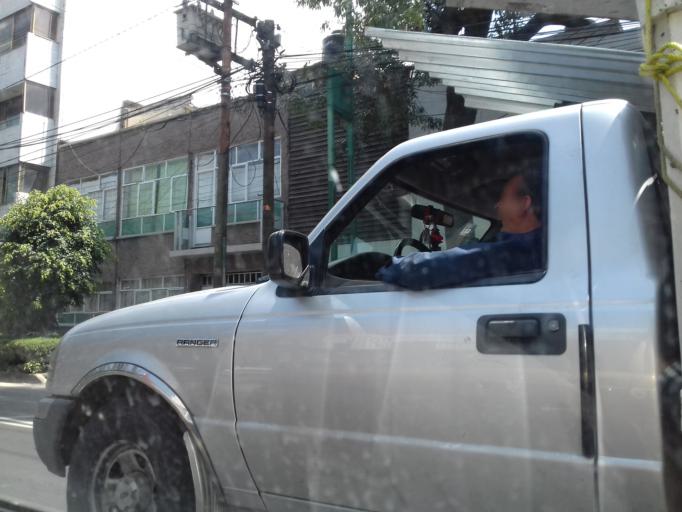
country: MX
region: Mexico City
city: Colonia del Valle
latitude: 19.3785
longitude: -99.1662
